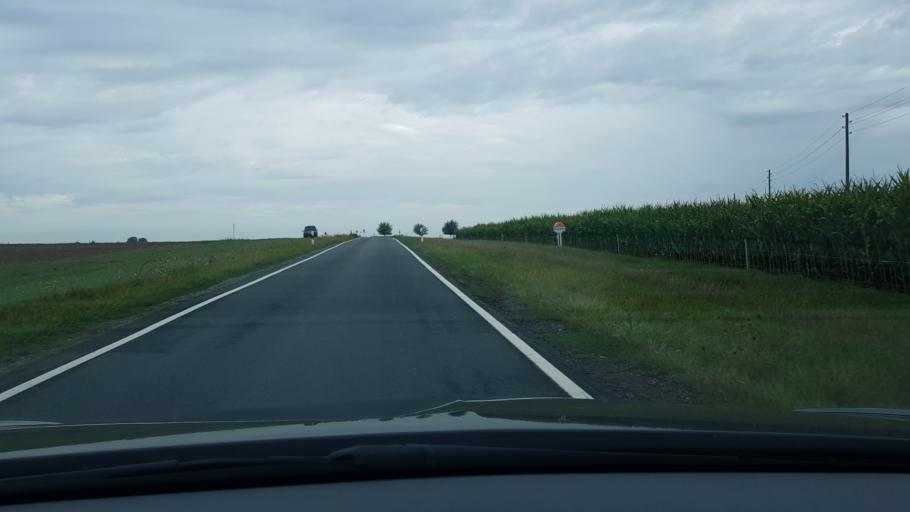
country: DE
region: Rheinland-Pfalz
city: Hatzenport
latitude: 50.2370
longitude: 7.4249
